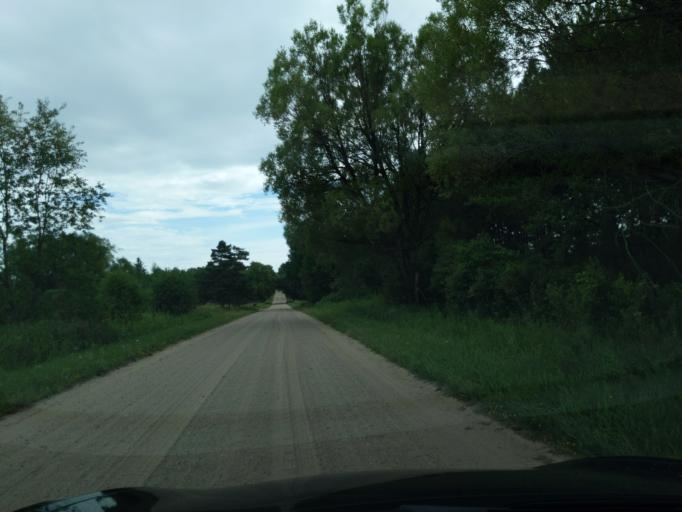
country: US
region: Michigan
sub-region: Clare County
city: Harrison
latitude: 43.9962
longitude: -85.0084
